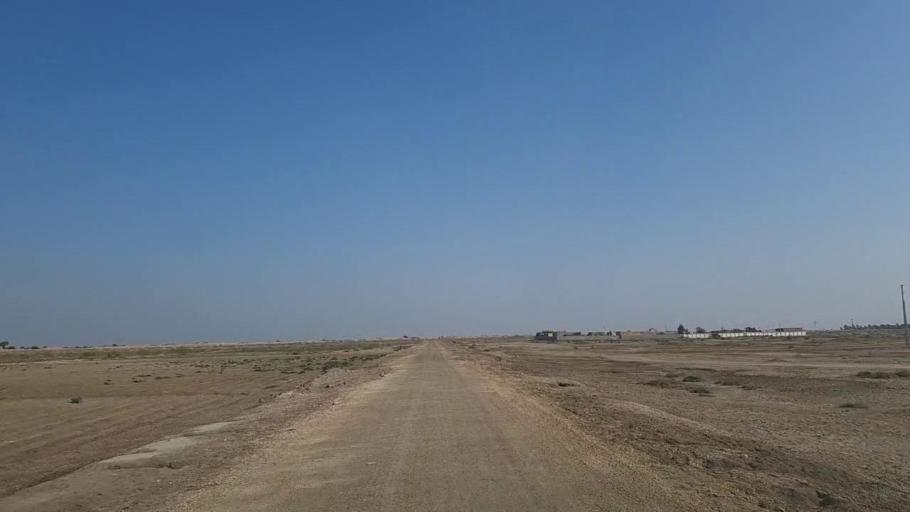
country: PK
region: Sindh
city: Digri
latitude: 25.0726
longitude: 69.2225
